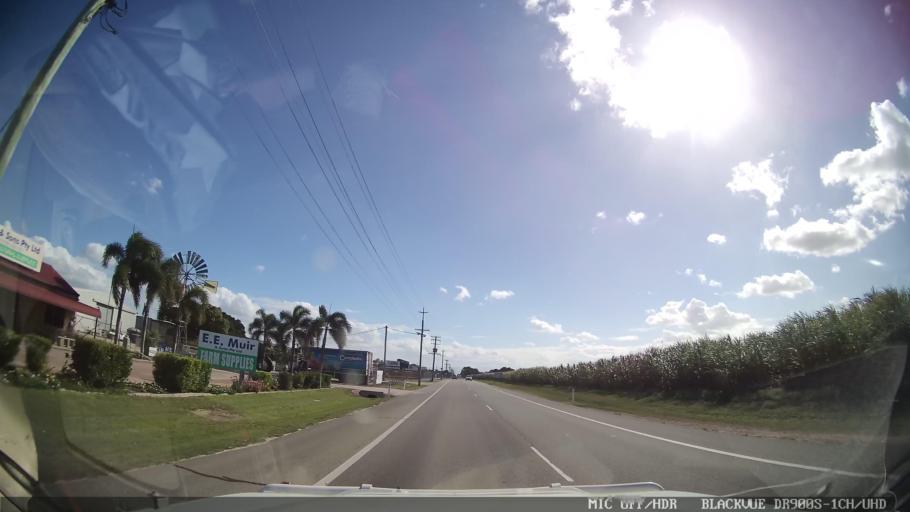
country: AU
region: Queensland
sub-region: Burdekin
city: Ayr
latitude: -19.5555
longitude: 147.3666
